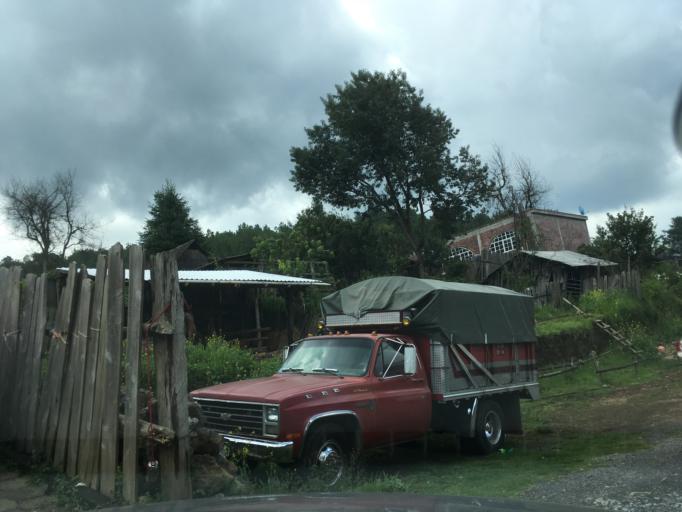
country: MX
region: Michoacan
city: Capacuaro
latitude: 19.5960
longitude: -102.0016
